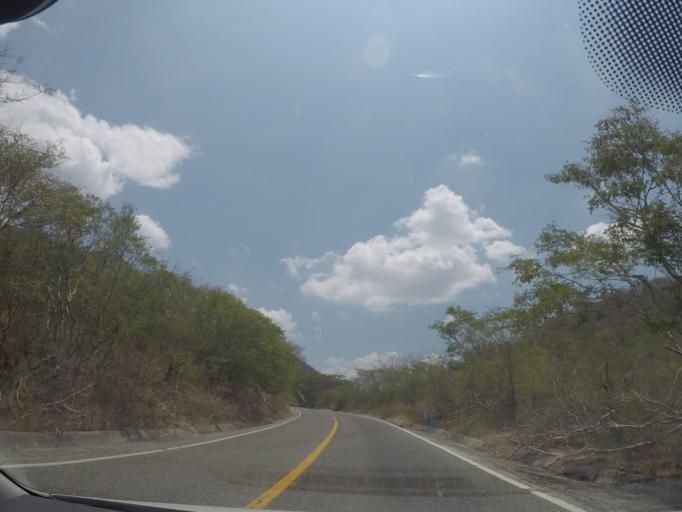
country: MX
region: Oaxaca
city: Santa Maria Jalapa del Marques
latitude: 16.3699
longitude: -95.3834
